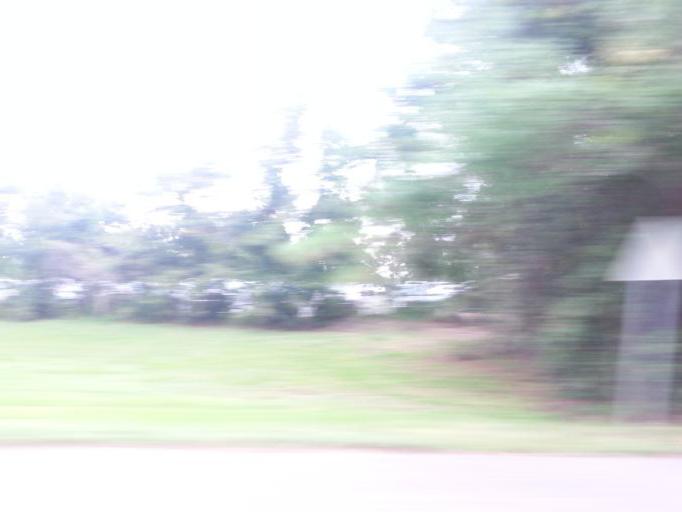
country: US
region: Alabama
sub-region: Baldwin County
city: Point Clear
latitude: 30.4831
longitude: -87.9308
